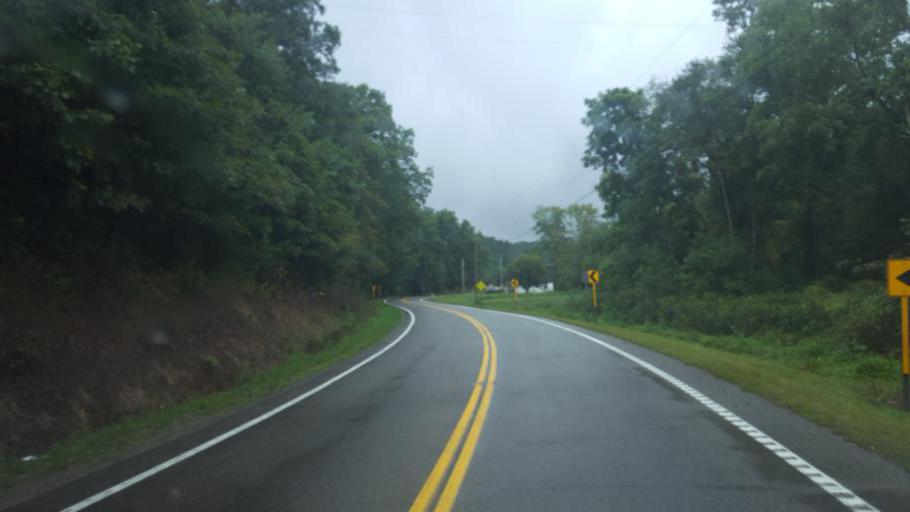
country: US
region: Ohio
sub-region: Jackson County
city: Oak Hill
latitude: 38.8511
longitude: -82.6312
